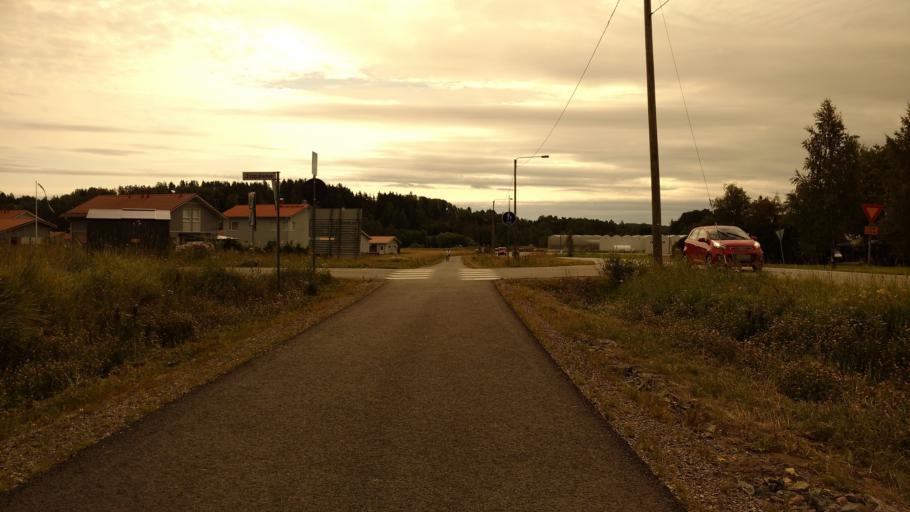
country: FI
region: Varsinais-Suomi
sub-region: Turku
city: Piikkioe
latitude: 60.4274
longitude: 22.4832
